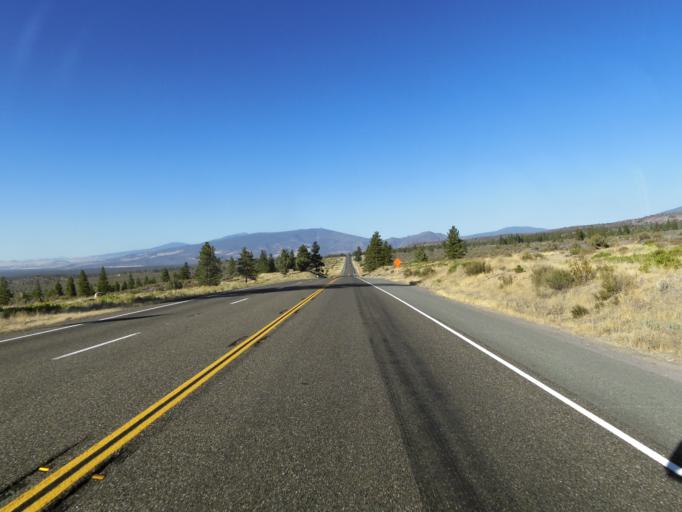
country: US
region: California
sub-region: Siskiyou County
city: Weed
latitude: 41.4840
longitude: -122.3414
